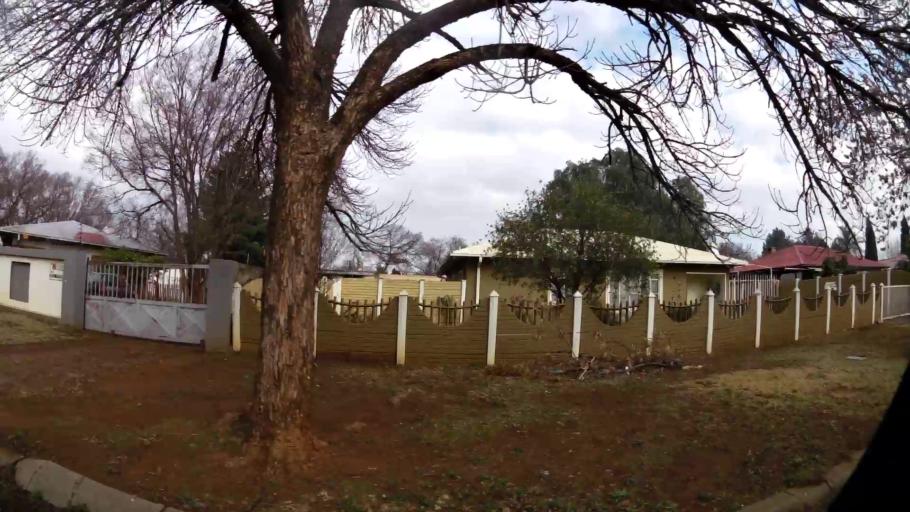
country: ZA
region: Gauteng
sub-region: Sedibeng District Municipality
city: Vanderbijlpark
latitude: -26.7014
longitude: 27.8304
